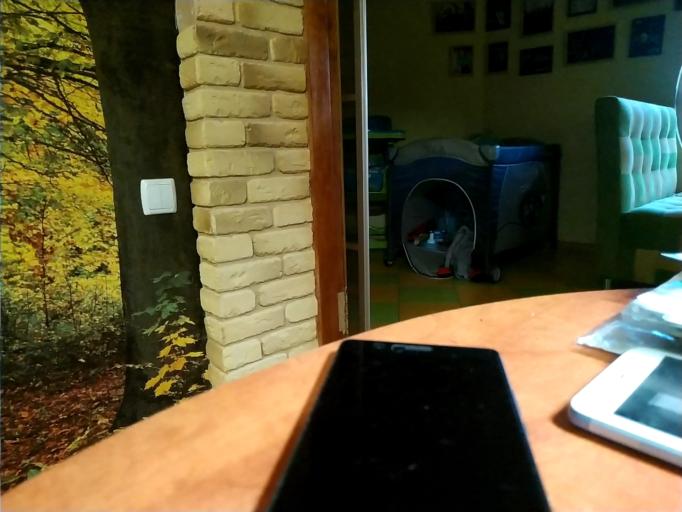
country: RU
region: Orjol
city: Znamenskoye
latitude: 53.4799
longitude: 35.5150
